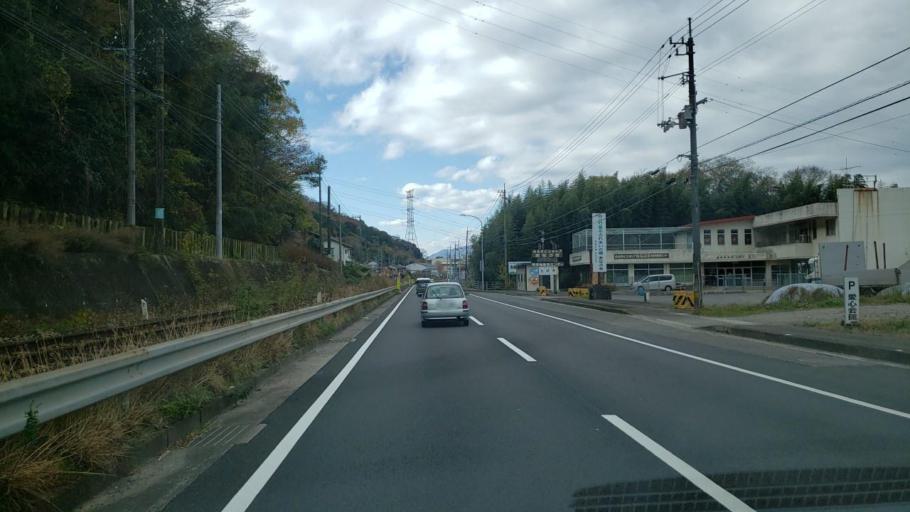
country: JP
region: Tokushima
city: Wakimachi
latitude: 34.0549
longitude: 134.1362
